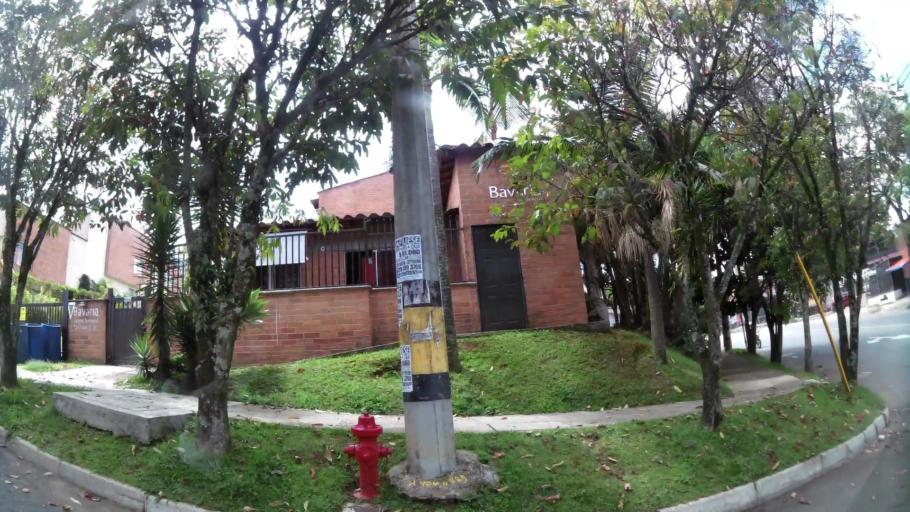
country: CO
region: Antioquia
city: La Estrella
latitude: 6.1595
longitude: -75.6367
